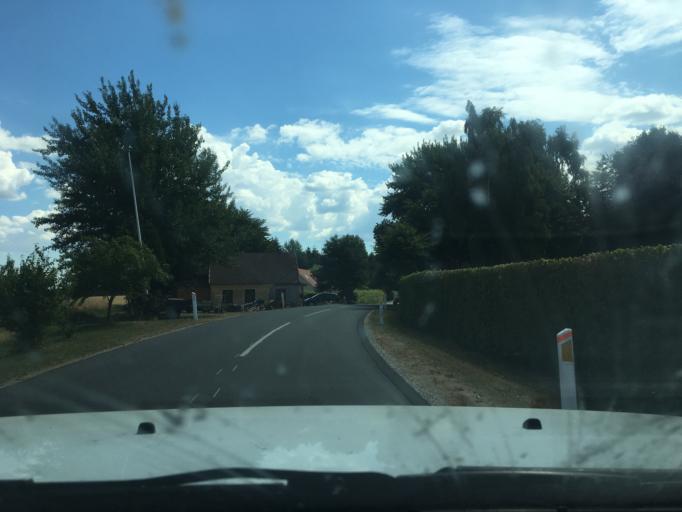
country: DK
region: Central Jutland
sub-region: Syddjurs Kommune
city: Hornslet
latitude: 56.3473
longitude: 10.2567
